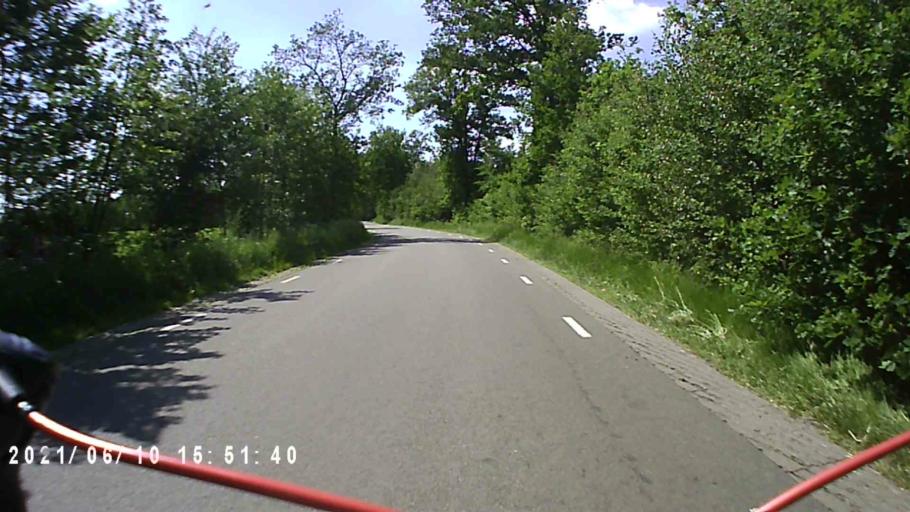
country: NL
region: Friesland
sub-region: Gemeente Achtkarspelen
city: Harkema
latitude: 53.1730
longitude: 6.1165
